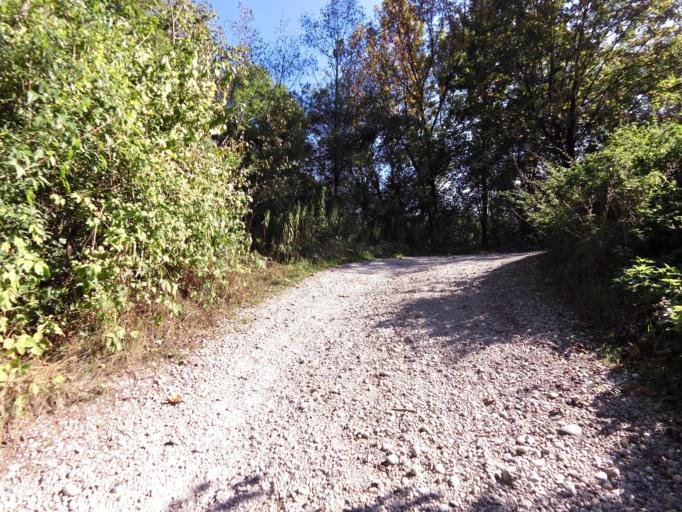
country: DE
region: Bavaria
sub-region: Lower Bavaria
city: Essenbach
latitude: 48.5874
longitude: 12.2310
